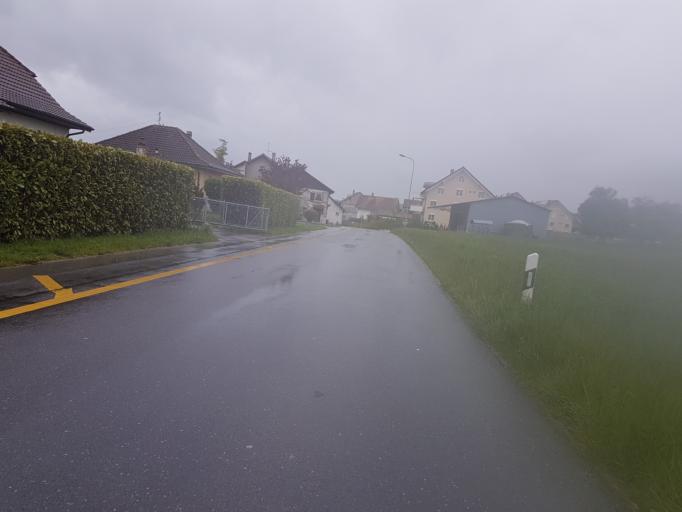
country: CH
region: Vaud
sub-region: Gros-de-Vaud District
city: Penthalaz
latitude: 46.6324
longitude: 6.5263
